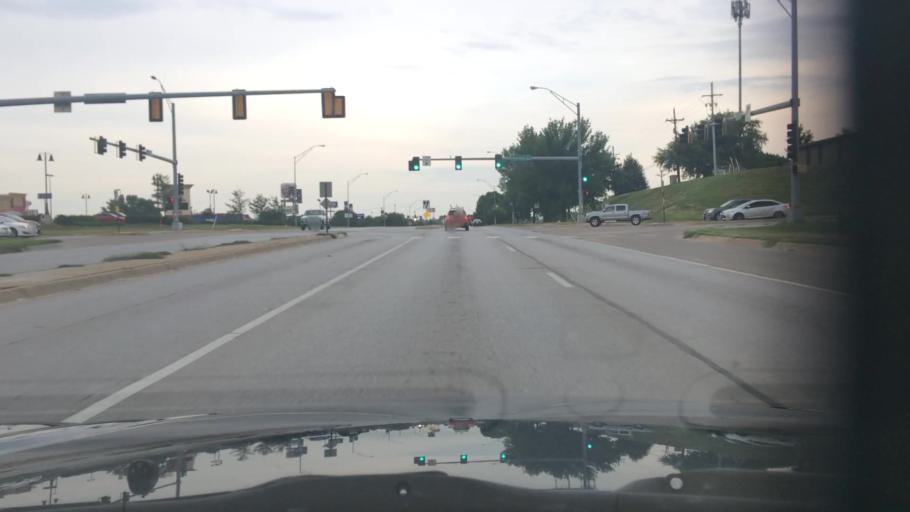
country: US
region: Nebraska
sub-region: Douglas County
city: Ralston
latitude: 41.1913
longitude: -96.0431
